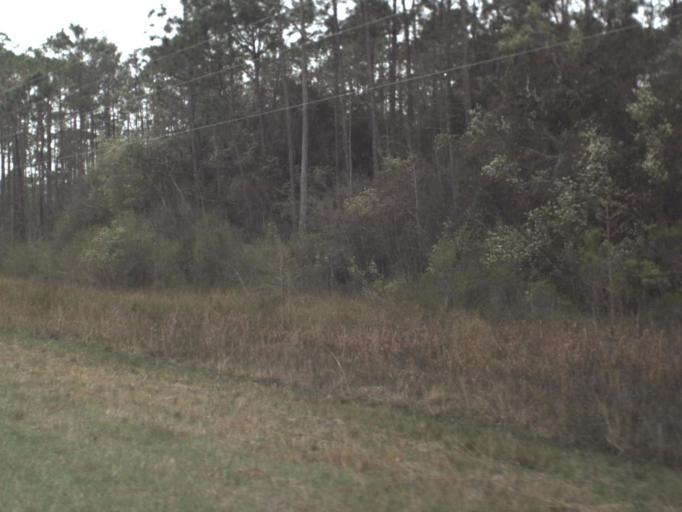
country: US
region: Florida
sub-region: Liberty County
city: Bristol
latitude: 30.2700
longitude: -84.8489
